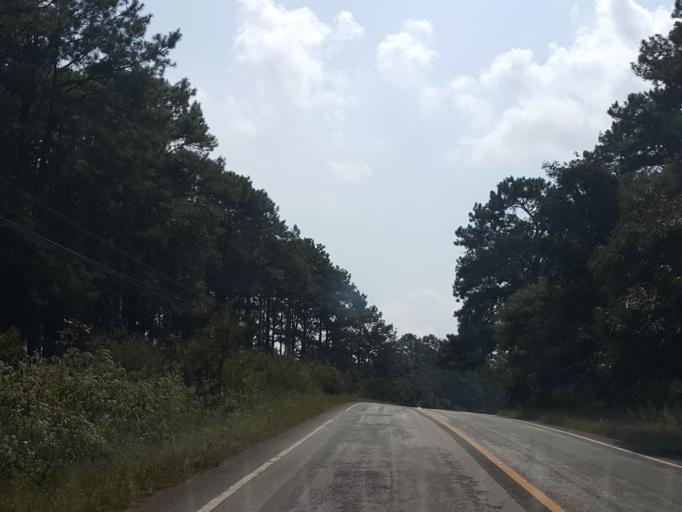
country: TH
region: Chiang Mai
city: Hot
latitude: 18.1299
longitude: 98.3762
